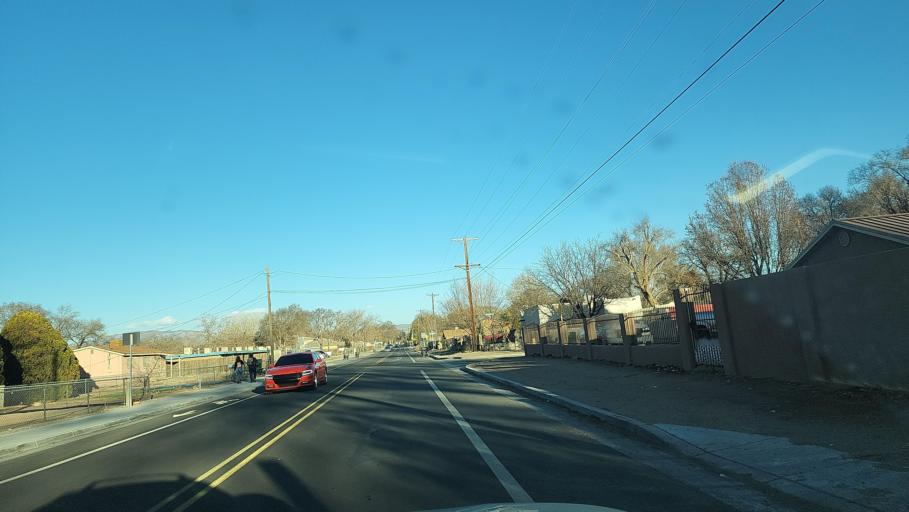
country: US
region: New Mexico
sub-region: Bernalillo County
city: South Valley
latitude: 35.0306
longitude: -106.6976
